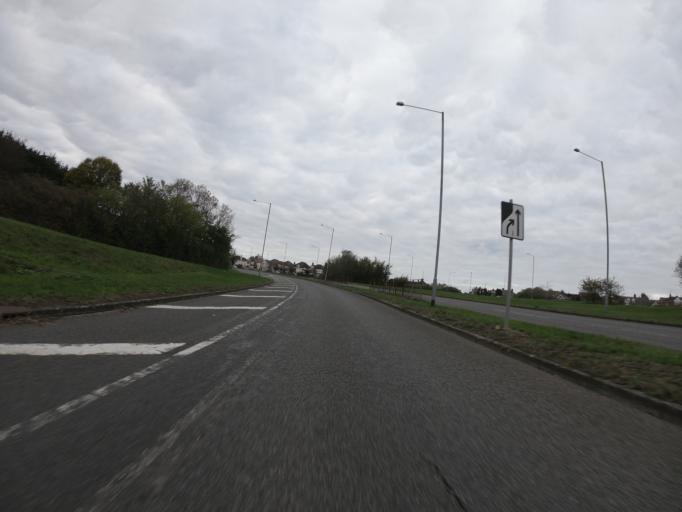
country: GB
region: England
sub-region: Borough of Thurrock
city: Chadwell St Mary
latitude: 51.4853
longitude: 0.3489
